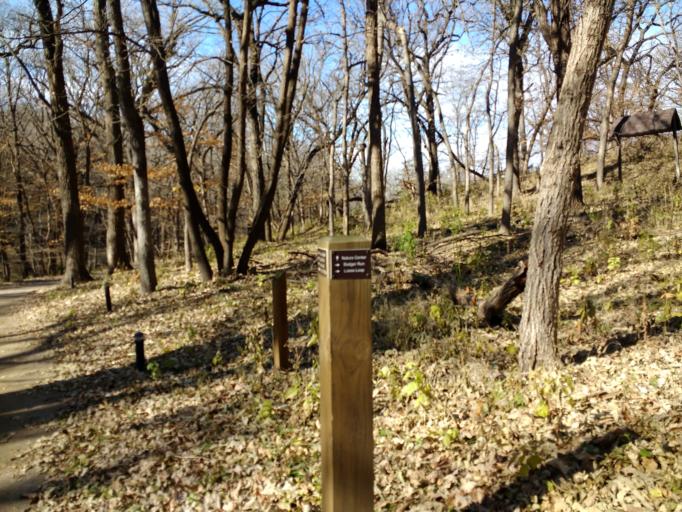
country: US
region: South Dakota
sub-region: Union County
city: North Sioux City
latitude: 42.5423
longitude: -96.4705
